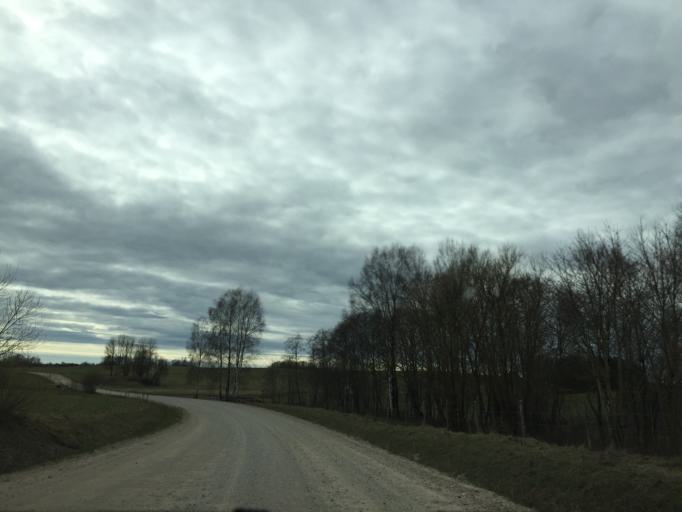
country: LT
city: Silale
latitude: 55.6184
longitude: 22.1931
